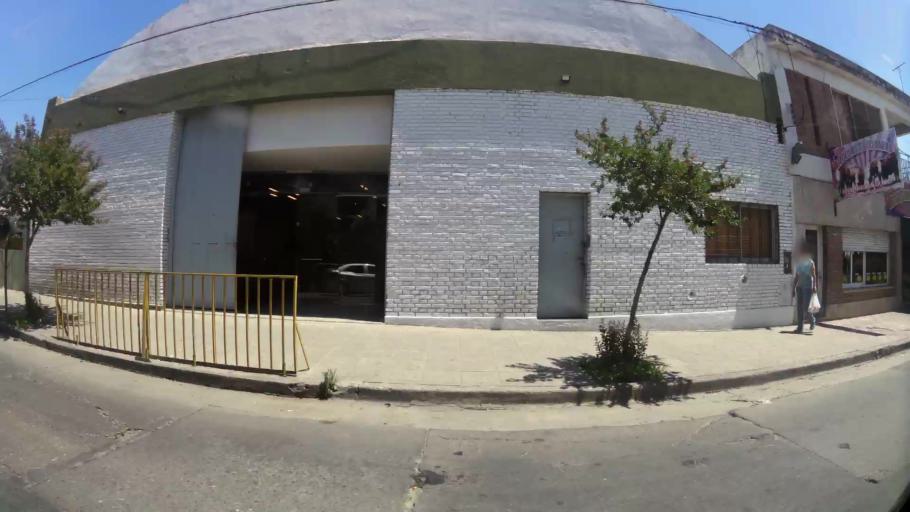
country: AR
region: Cordoba
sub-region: Departamento de Capital
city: Cordoba
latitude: -31.3971
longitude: -64.2093
